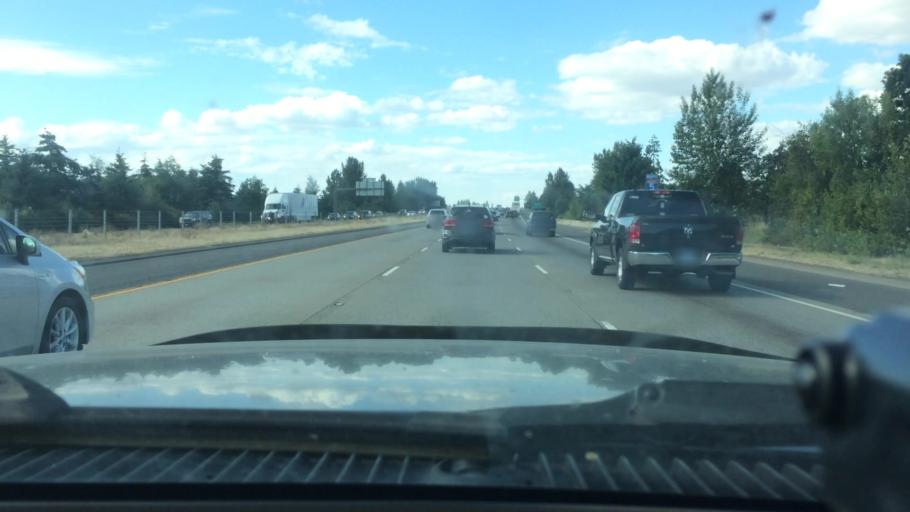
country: US
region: Oregon
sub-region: Marion County
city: Four Corners
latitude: 44.9229
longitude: -122.9902
